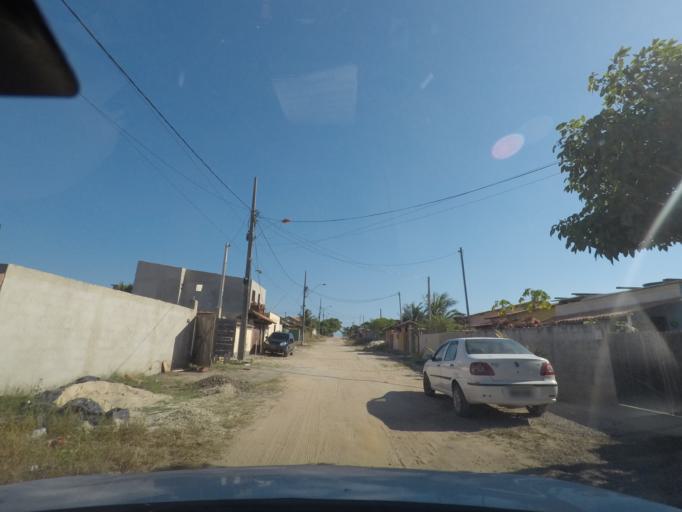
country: BR
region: Rio de Janeiro
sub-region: Marica
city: Marica
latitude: -22.9673
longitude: -42.9172
